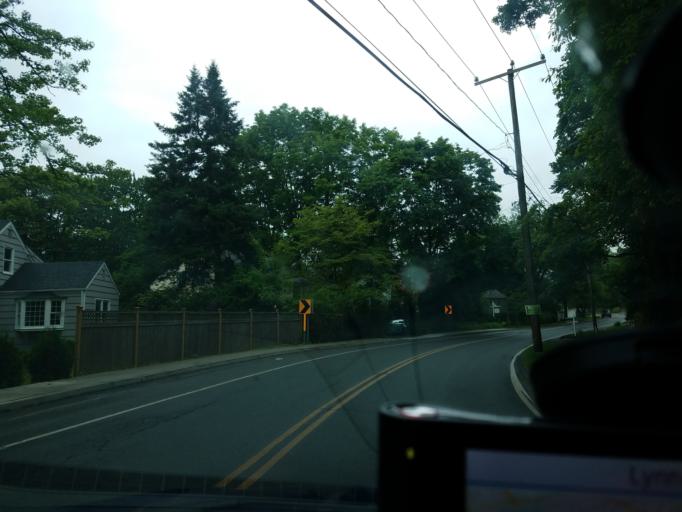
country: US
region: Connecticut
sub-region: Fairfield County
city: Stamford
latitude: 41.0877
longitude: -73.5125
